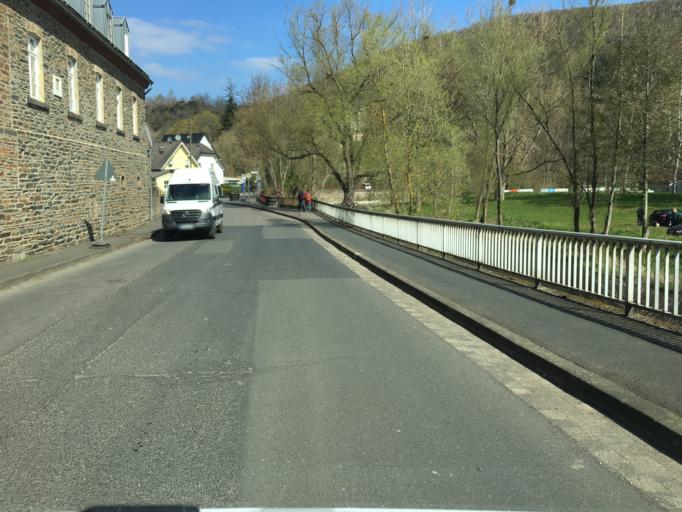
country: DE
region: Rheinland-Pfalz
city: Altenahr
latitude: 50.5094
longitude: 6.9763
